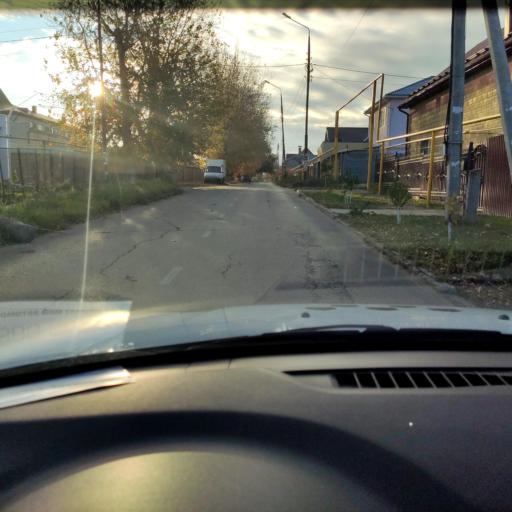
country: RU
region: Samara
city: Tol'yatti
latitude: 53.5250
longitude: 49.4043
